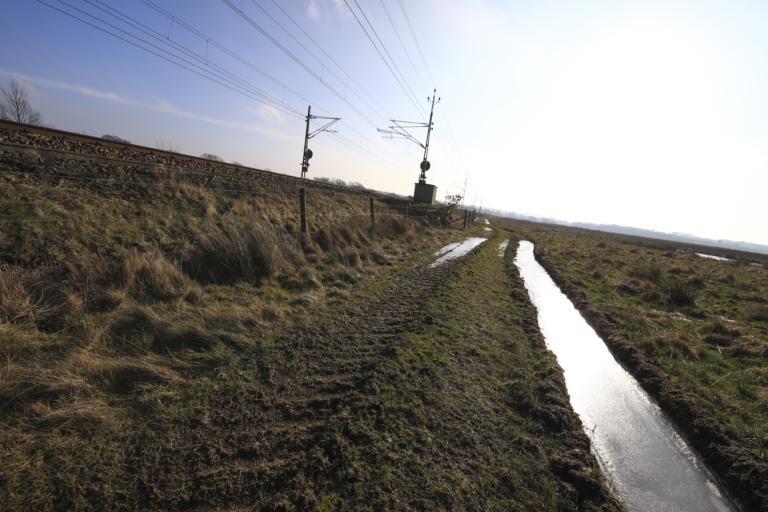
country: SE
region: Halland
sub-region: Kungsbacka Kommun
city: Frillesas
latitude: 57.2209
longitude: 12.2175
